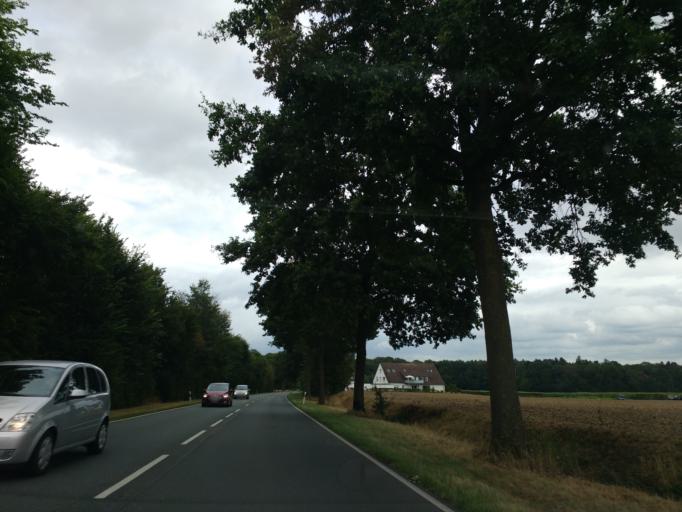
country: DE
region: Lower Saxony
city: Bad Rothenfelde
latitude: 52.1044
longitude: 8.1452
